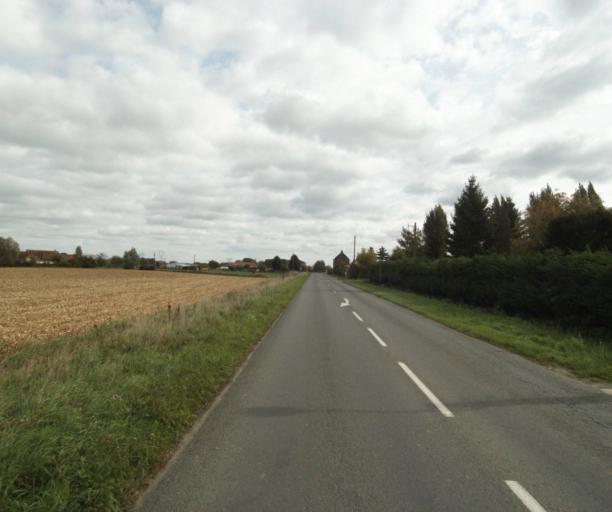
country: FR
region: Nord-Pas-de-Calais
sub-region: Departement du Pas-de-Calais
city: Fleurbaix
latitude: 50.6553
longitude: 2.8452
